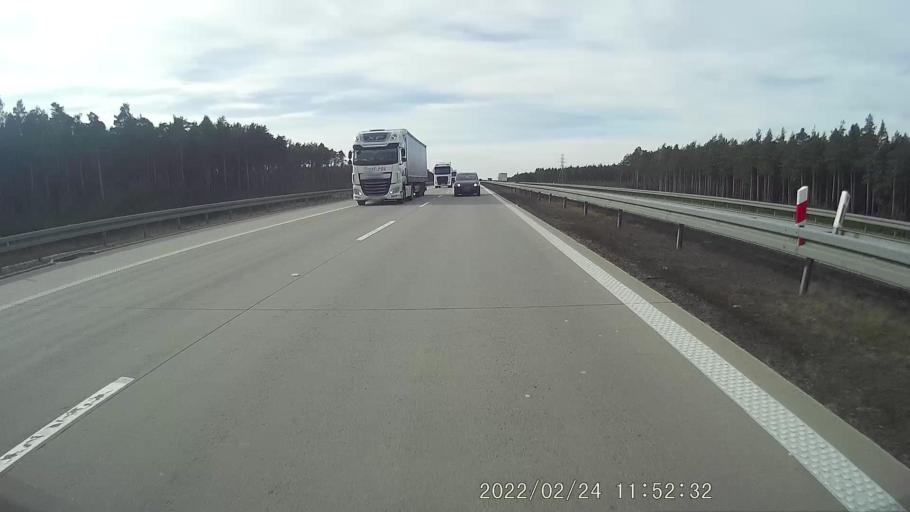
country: PL
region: Lower Silesian Voivodeship
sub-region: Powiat polkowicki
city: Radwanice
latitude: 51.6217
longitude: 15.9773
